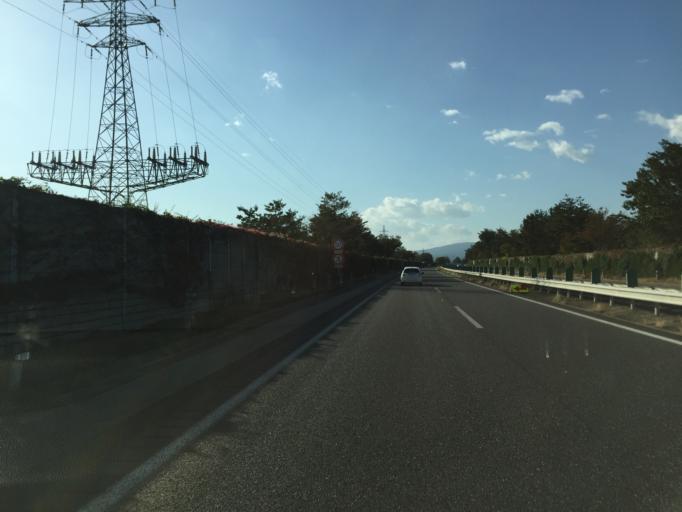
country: JP
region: Fukushima
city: Fukushima-shi
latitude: 37.7729
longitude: 140.4130
